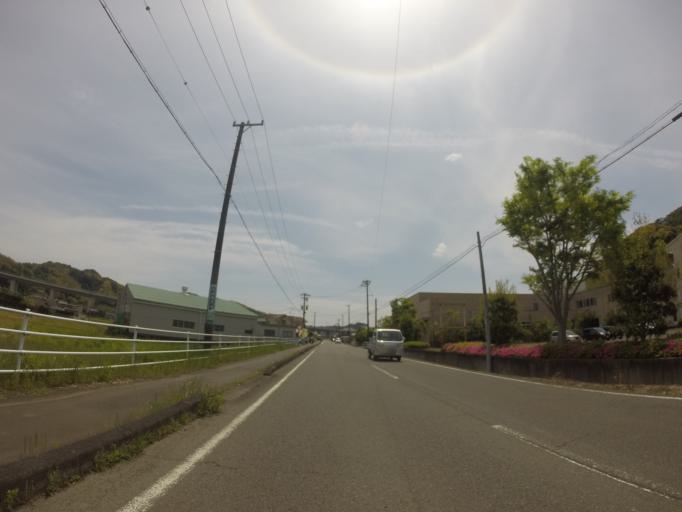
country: JP
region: Shizuoka
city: Fujieda
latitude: 34.9092
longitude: 138.2468
